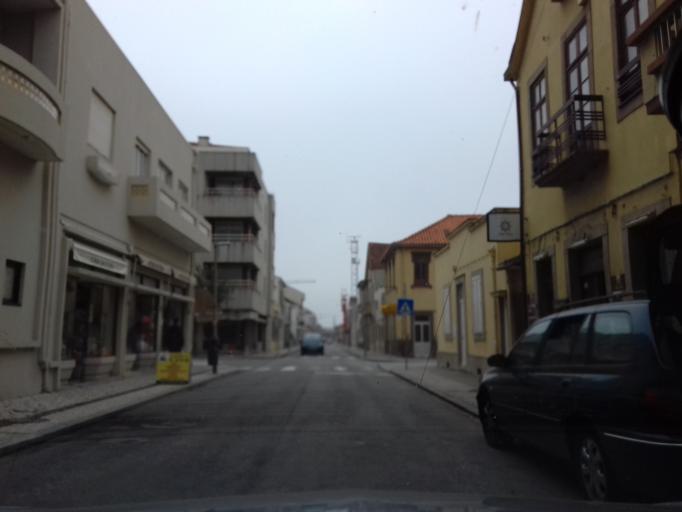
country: PT
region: Aveiro
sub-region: Espinho
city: Espinho
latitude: 41.0075
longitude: -8.6454
